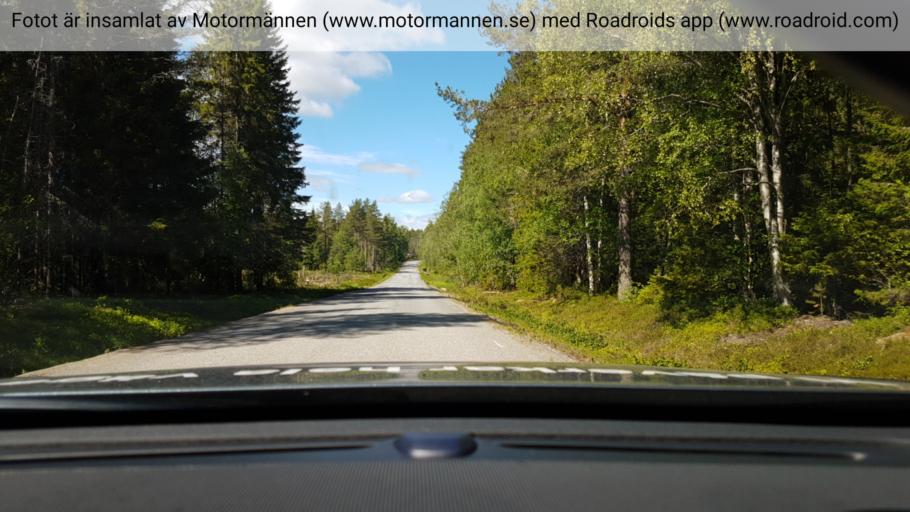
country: SE
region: Vaesterbotten
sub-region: Skelleftea Kommun
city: Burea
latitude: 64.4465
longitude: 21.4754
